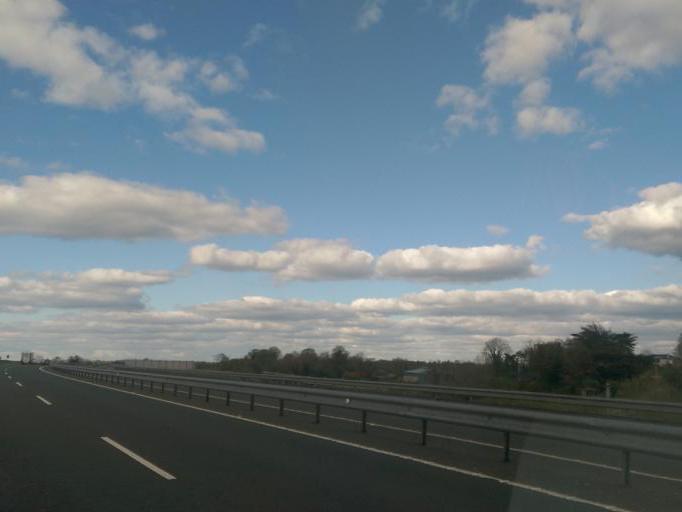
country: IE
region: Leinster
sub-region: An Iarmhi
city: Athlone
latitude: 53.3968
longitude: -8.0484
